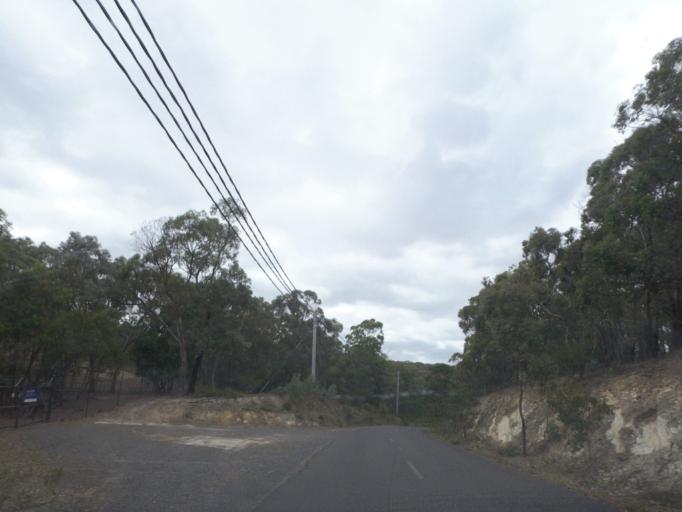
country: AU
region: Victoria
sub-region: Yarra Ranges
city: Chirnside Park
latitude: -37.6832
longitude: 145.3107
